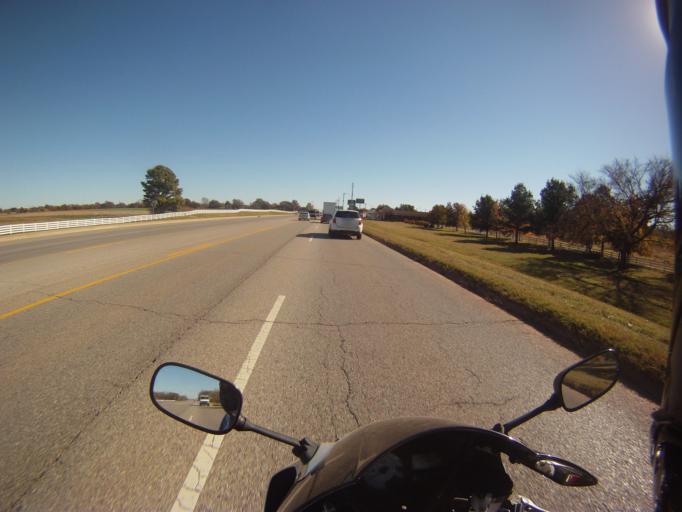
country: US
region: Oklahoma
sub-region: Payne County
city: Stillwater
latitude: 36.1158
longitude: -97.0935
